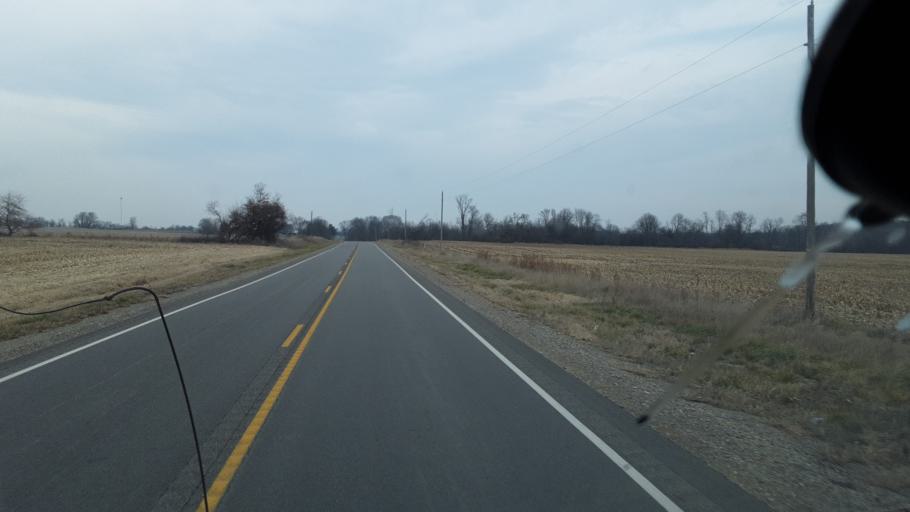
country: US
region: Indiana
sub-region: Steuben County
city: Angola
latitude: 41.6094
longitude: -85.1693
